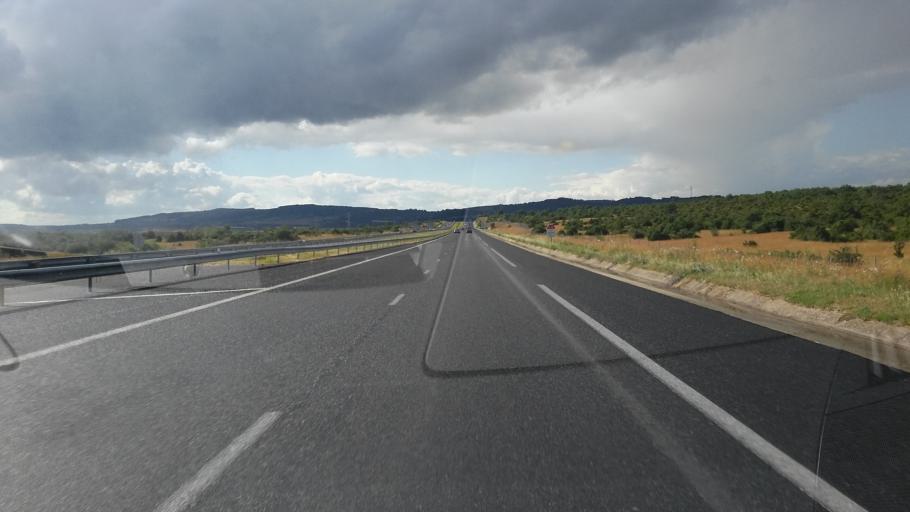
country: FR
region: Midi-Pyrenees
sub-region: Departement de l'Aveyron
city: La Cavalerie
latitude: 43.9361
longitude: 3.2294
